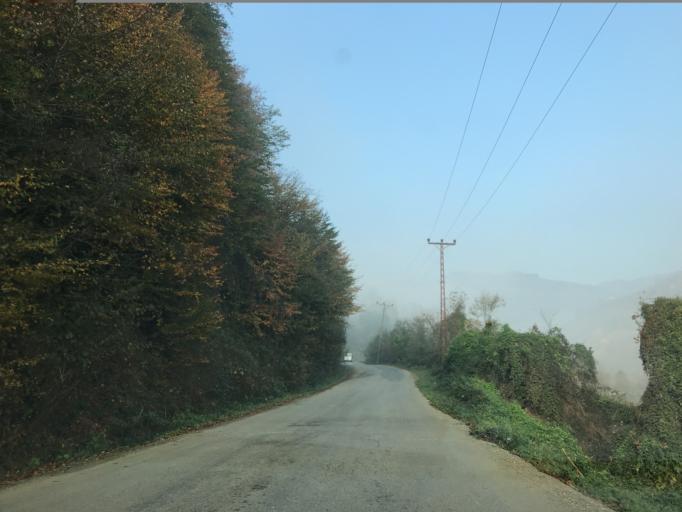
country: TR
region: Duzce
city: Cumayeri
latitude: 40.9142
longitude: 30.9377
